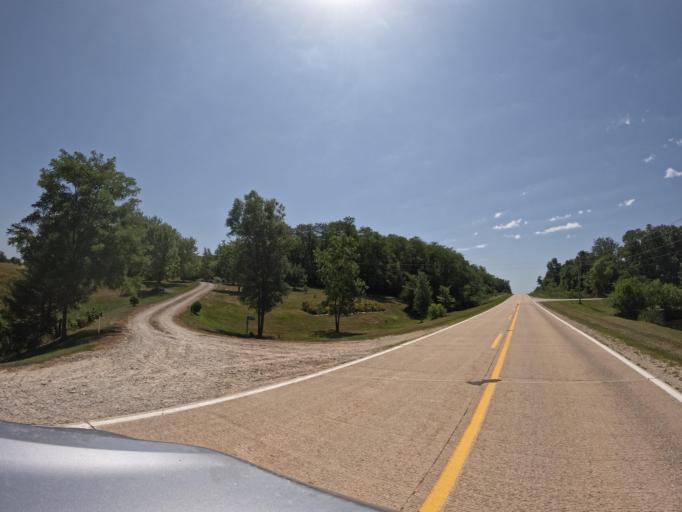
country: US
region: Iowa
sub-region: Henry County
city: Mount Pleasant
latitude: 40.9164
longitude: -91.5542
